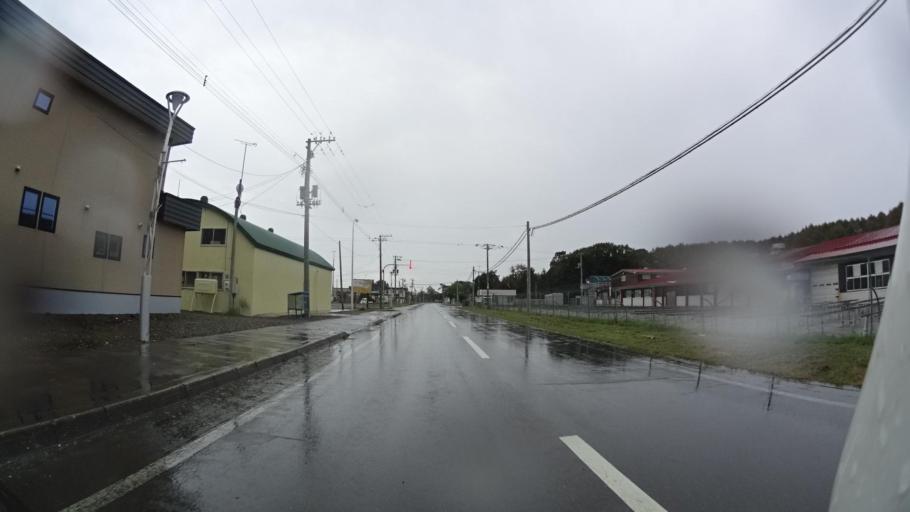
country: JP
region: Hokkaido
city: Kitami
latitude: 44.1884
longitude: 143.7399
